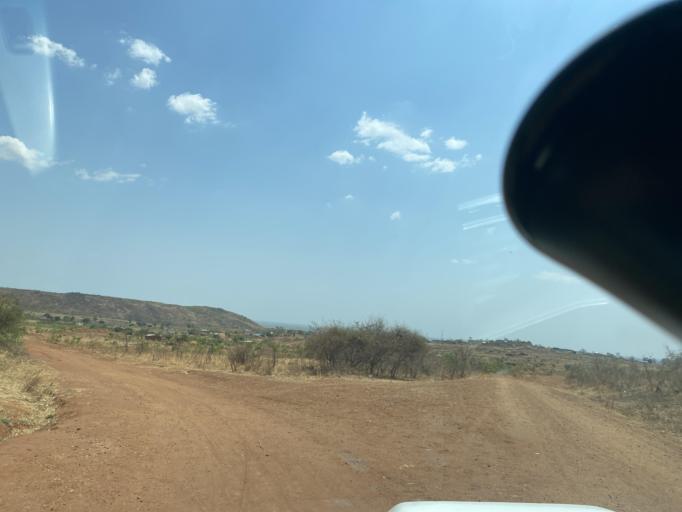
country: ZM
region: Lusaka
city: Lusaka
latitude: -15.5003
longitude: 27.9447
